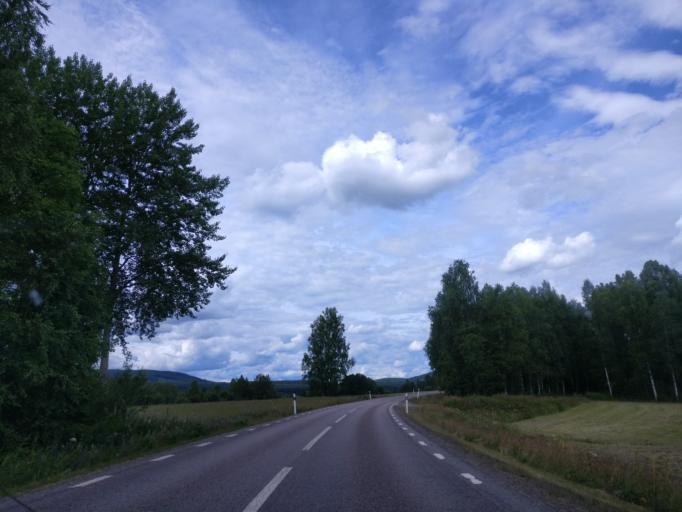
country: SE
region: Vaermland
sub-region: Hagfors Kommun
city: Ekshaerad
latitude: 60.1540
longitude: 13.4256
